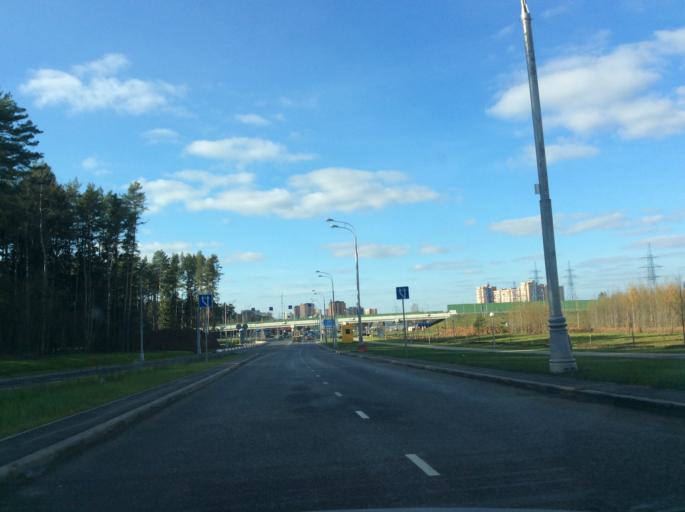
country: RU
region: Moskovskaya
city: Vatutinki
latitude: 55.4850
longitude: 37.3293
